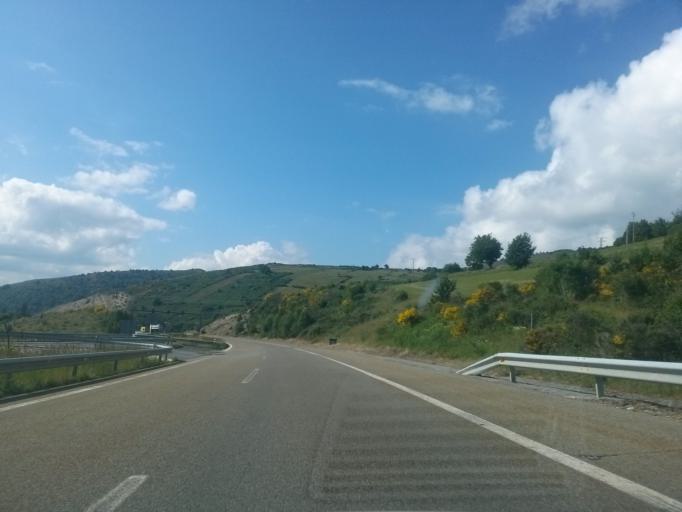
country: ES
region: Castille and Leon
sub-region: Provincia de Leon
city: Balboa
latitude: 42.7381
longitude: -7.0468
